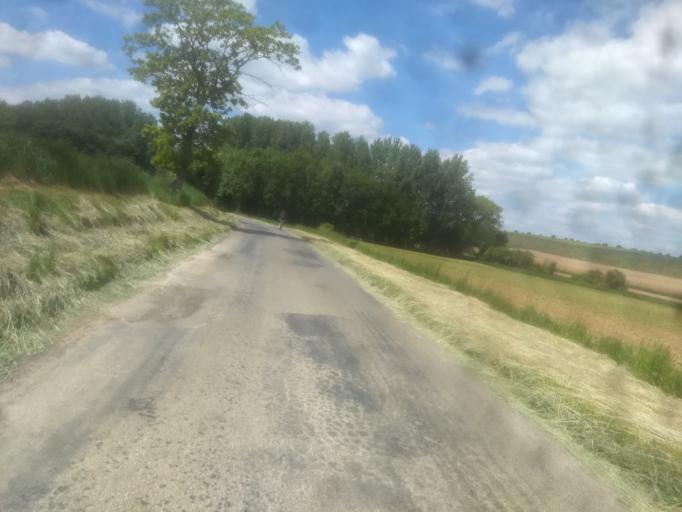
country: FR
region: Nord-Pas-de-Calais
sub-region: Departement du Pas-de-Calais
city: Beaumetz-les-Loges
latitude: 50.2261
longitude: 2.6629
